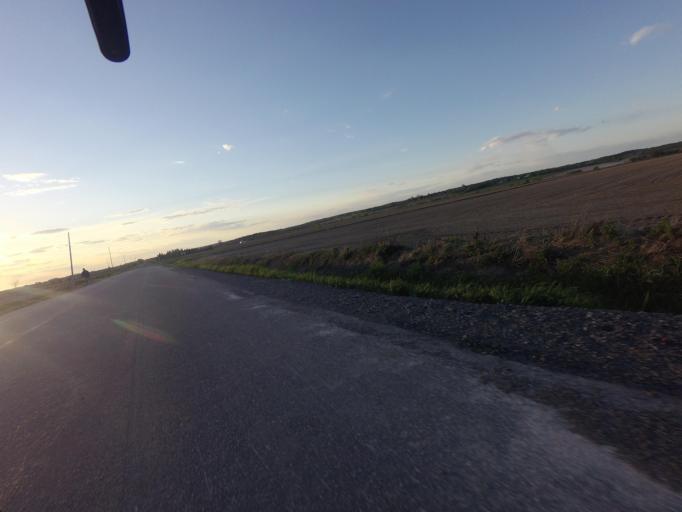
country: CA
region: Ontario
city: Arnprior
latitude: 45.3662
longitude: -76.1327
